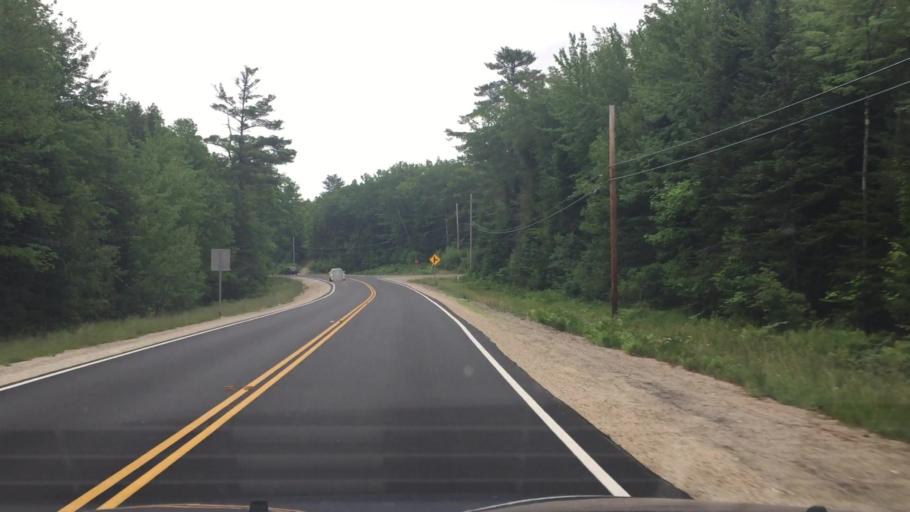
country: US
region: New Hampshire
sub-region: Carroll County
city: Freedom
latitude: 43.8075
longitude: -71.0646
